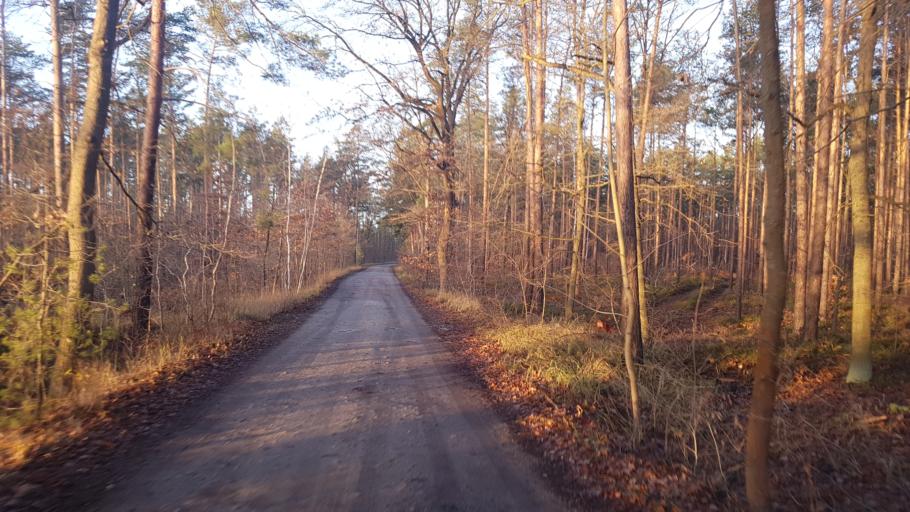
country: DE
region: Brandenburg
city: Ruckersdorf
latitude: 51.5925
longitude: 13.5815
